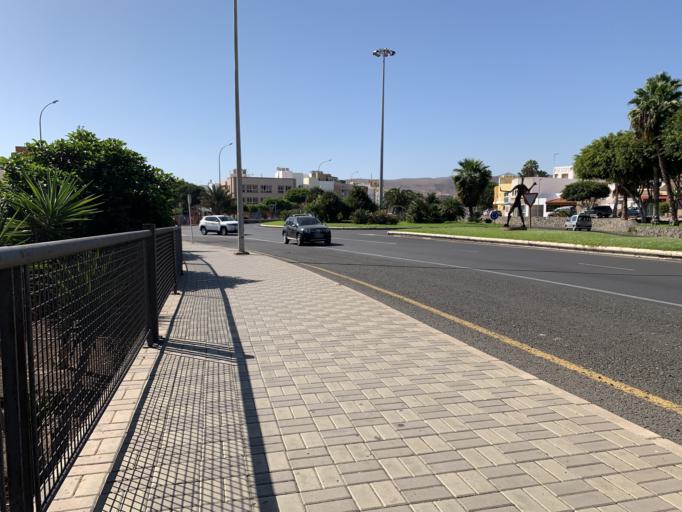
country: ES
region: Canary Islands
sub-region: Provincia de Las Palmas
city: Puerto del Rosario
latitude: 28.4958
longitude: -13.8643
